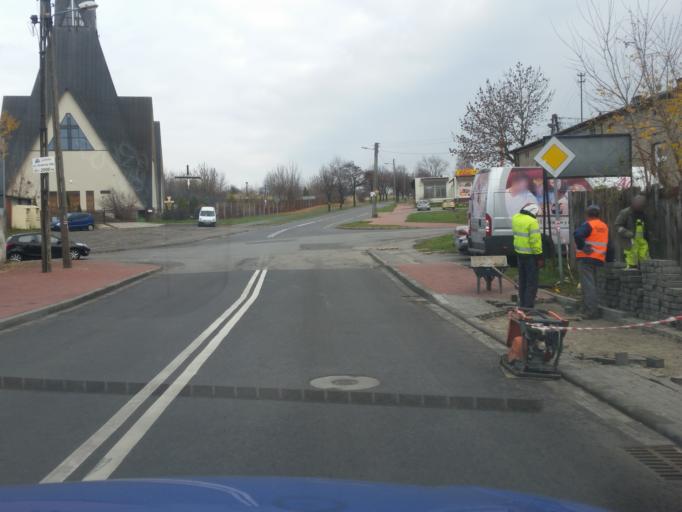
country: PL
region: Silesian Voivodeship
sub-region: Czestochowa
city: Czestochowa
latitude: 50.8139
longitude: 19.1433
